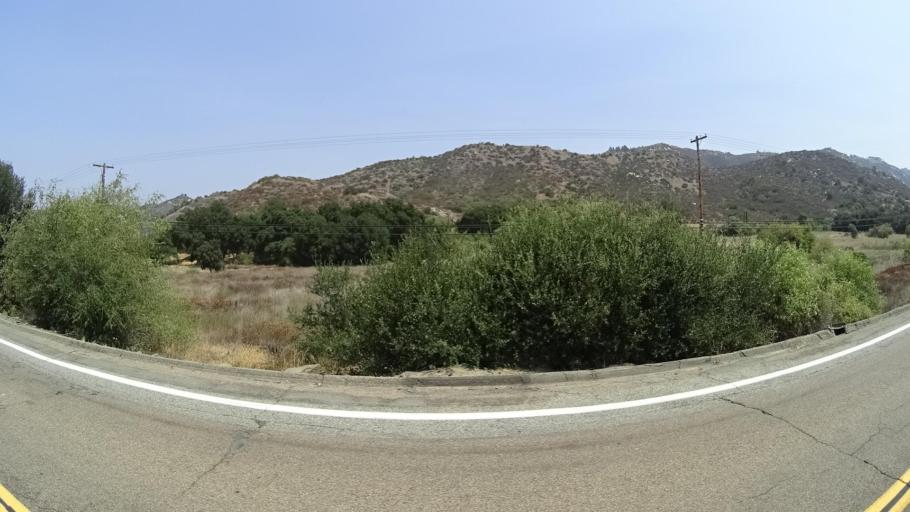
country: US
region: California
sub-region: San Diego County
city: Hidden Meadows
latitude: 33.2443
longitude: -117.1493
